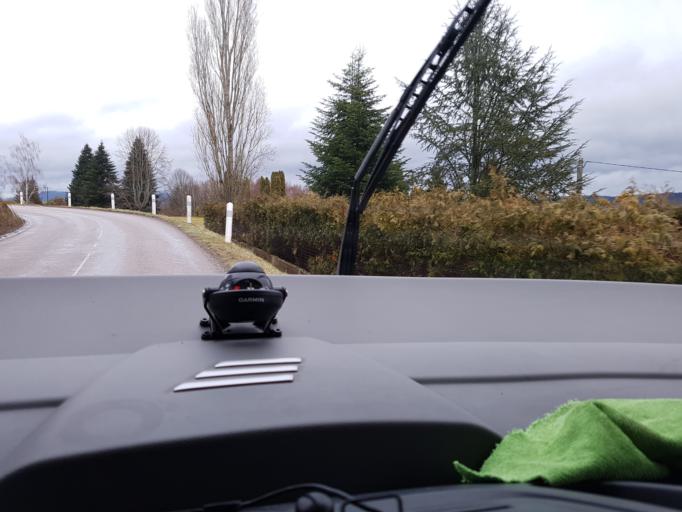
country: FR
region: Lorraine
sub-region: Departement des Vosges
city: Saint-Michel-sur-Meurthe
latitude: 48.3104
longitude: 6.8958
